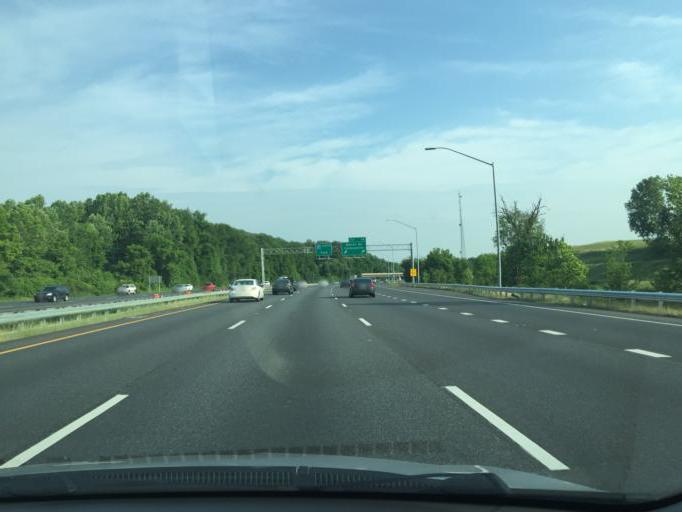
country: US
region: Maryland
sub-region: Baltimore County
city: Cockeysville
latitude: 39.4646
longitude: -76.6603
